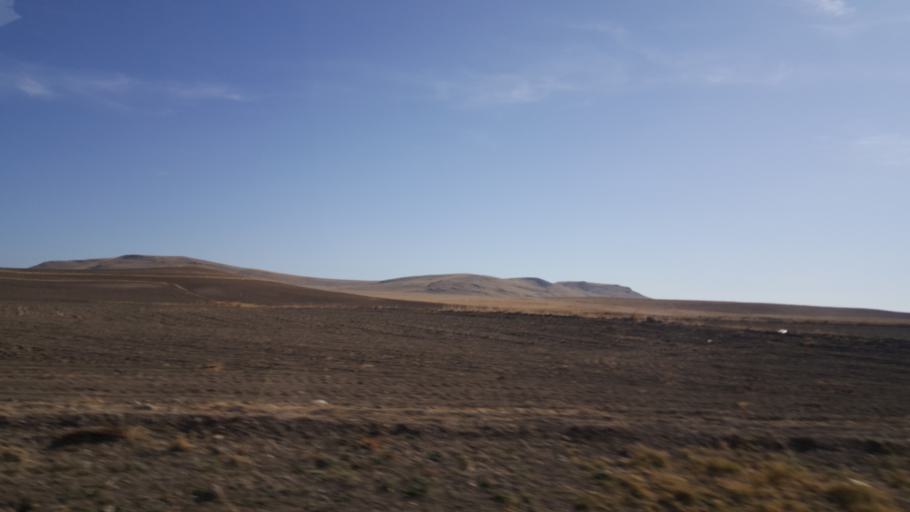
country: TR
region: Ankara
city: Yenice
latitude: 39.3542
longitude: 32.7881
